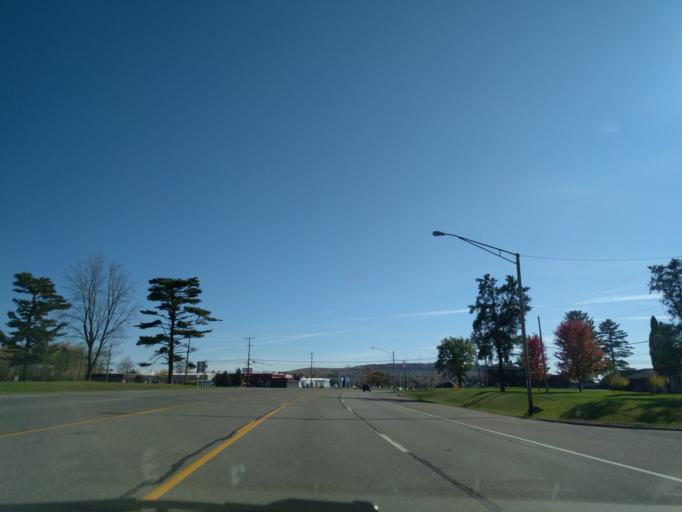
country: US
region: Michigan
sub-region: Dickinson County
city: Iron Mountain
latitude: 45.8462
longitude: -88.0498
